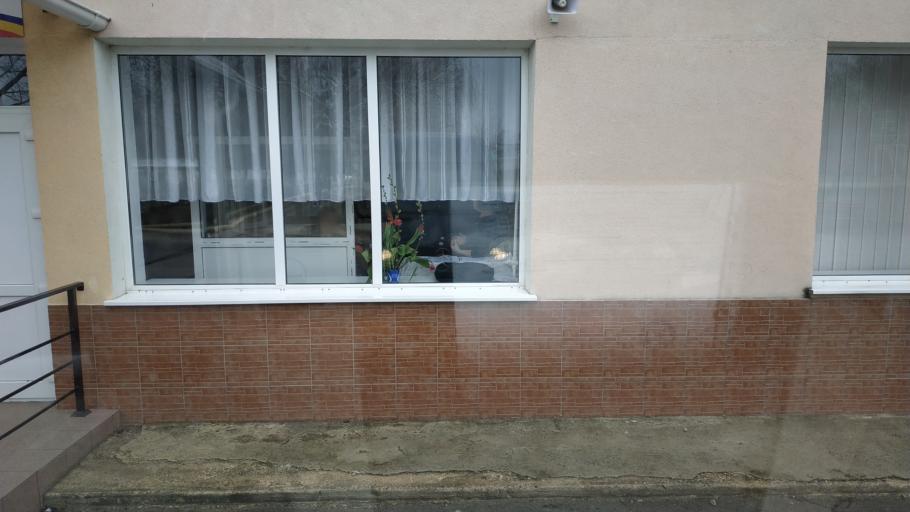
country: MD
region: Chisinau
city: Vatra
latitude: 47.0172
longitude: 28.7558
